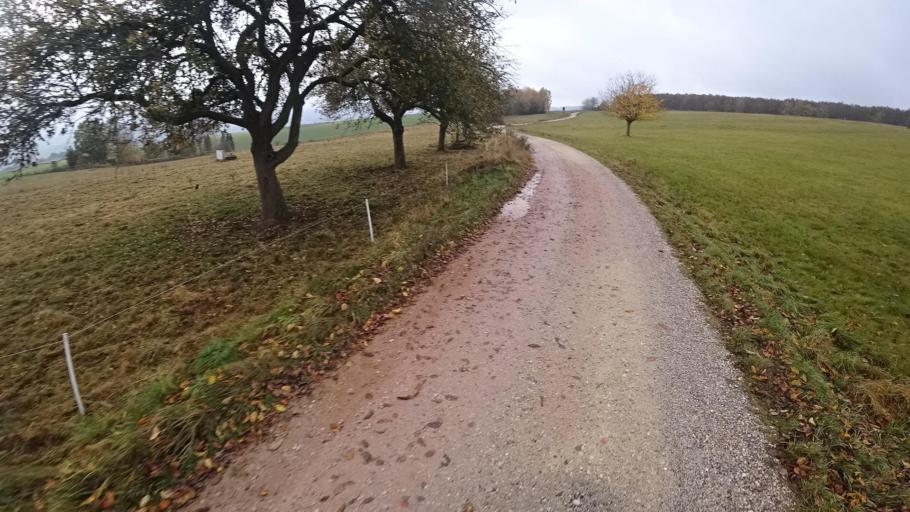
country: DE
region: Rheinland-Pfalz
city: Urbar
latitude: 50.1262
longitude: 7.7075
